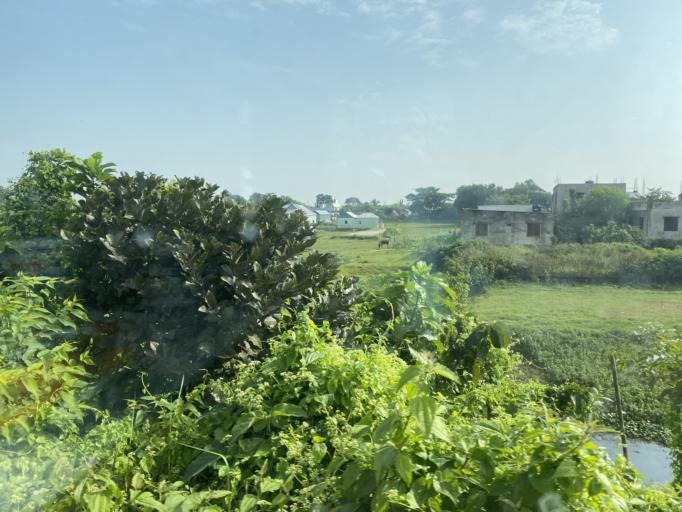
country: BD
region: Chittagong
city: Nabinagar
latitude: 23.9602
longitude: 91.1190
